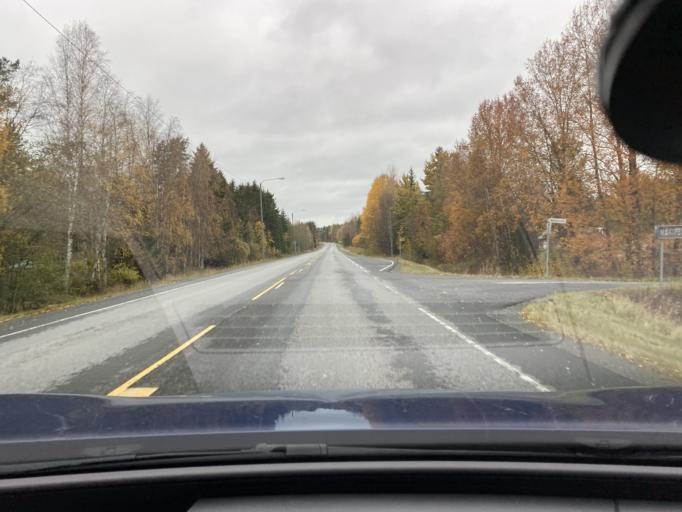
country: FI
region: Satakunta
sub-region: Rauma
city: Rauma
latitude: 61.1301
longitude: 21.6017
